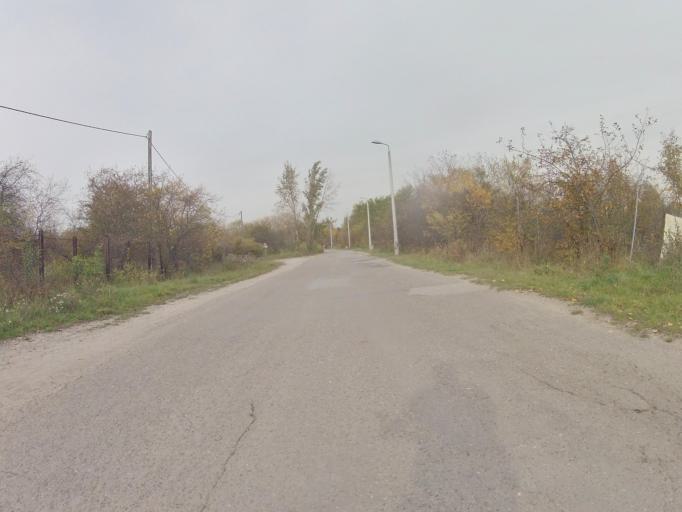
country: PL
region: Lesser Poland Voivodeship
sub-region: Krakow
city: Krakow
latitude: 50.0343
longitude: 19.9130
